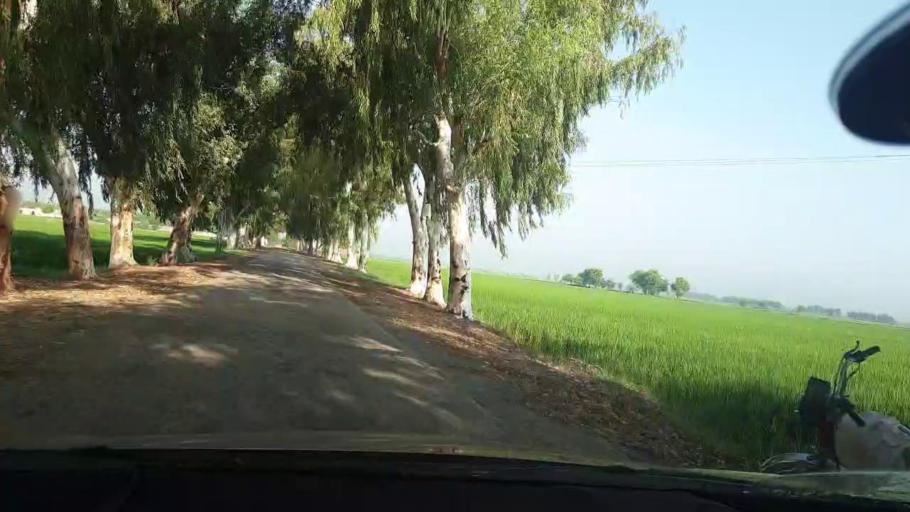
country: PK
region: Sindh
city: Kambar
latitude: 27.6520
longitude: 68.0376
